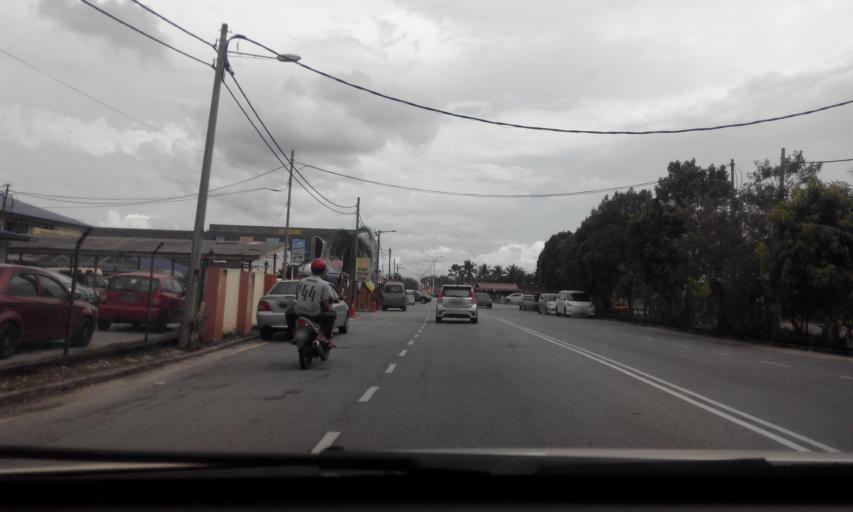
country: MY
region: Perak
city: Parit Buntar
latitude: 5.1306
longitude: 100.4818
